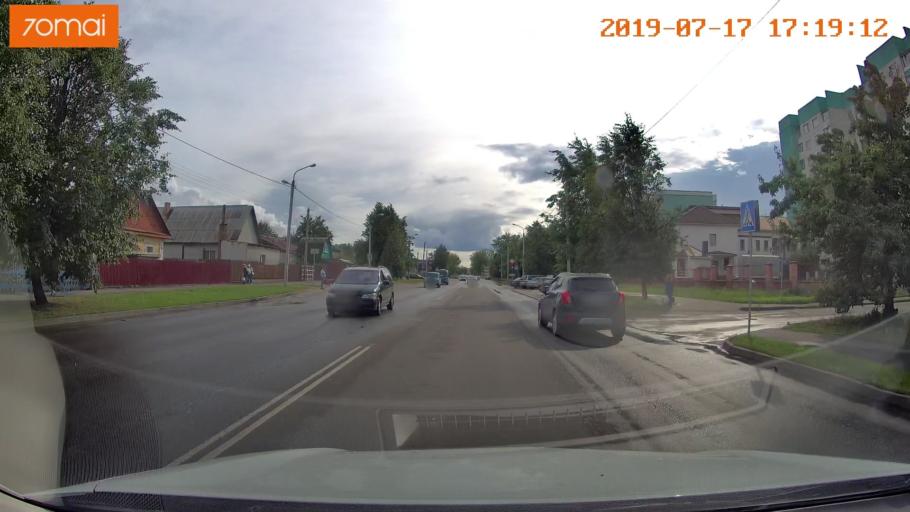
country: BY
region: Mogilev
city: Babruysk
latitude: 53.1579
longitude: 29.1936
